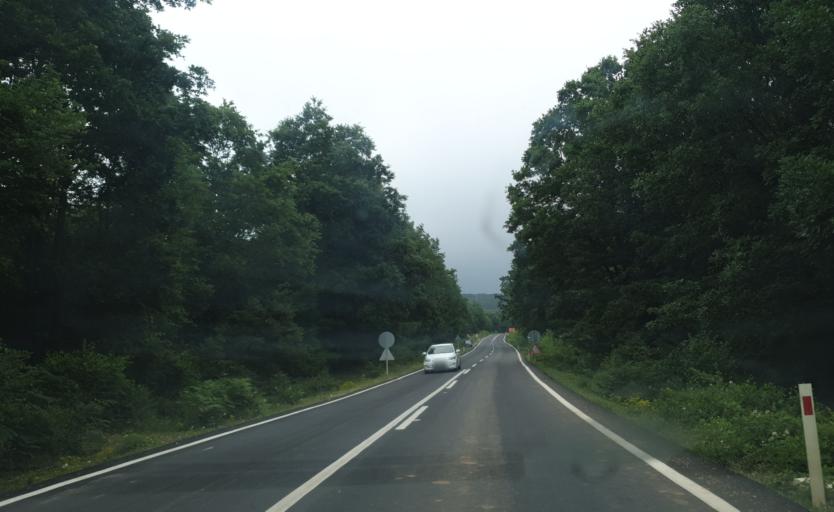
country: TR
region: Kirklareli
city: Salmydessus
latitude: 41.5939
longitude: 28.0777
